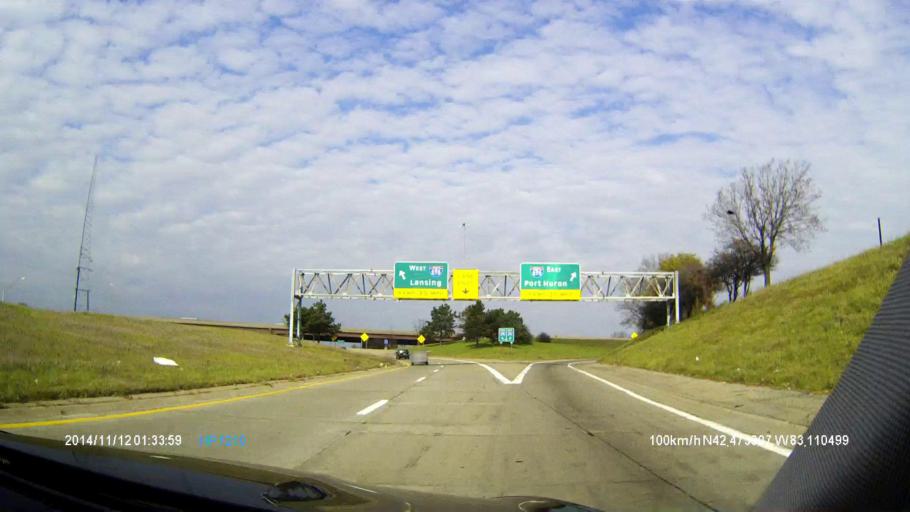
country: US
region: Michigan
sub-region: Oakland County
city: Hazel Park
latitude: 42.4739
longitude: -83.1105
